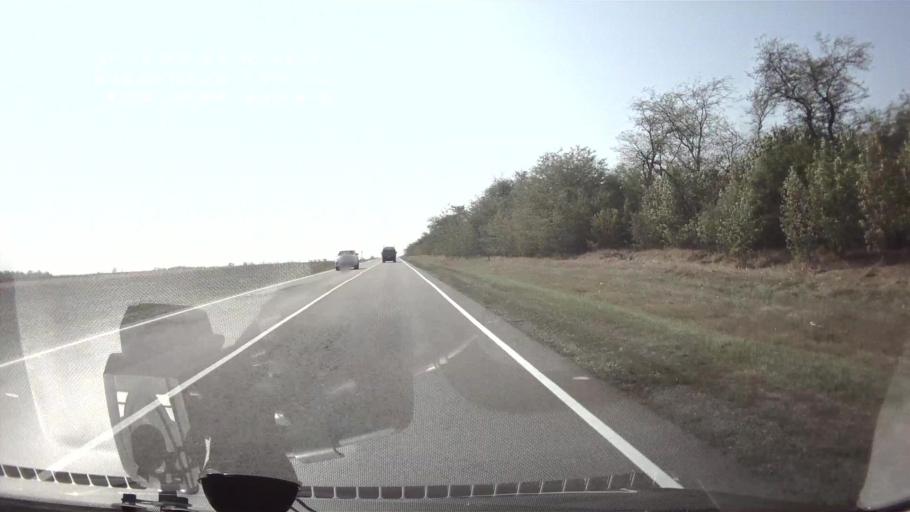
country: RU
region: Krasnodarskiy
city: Novopokrovskaya
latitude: 45.8311
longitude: 40.7202
